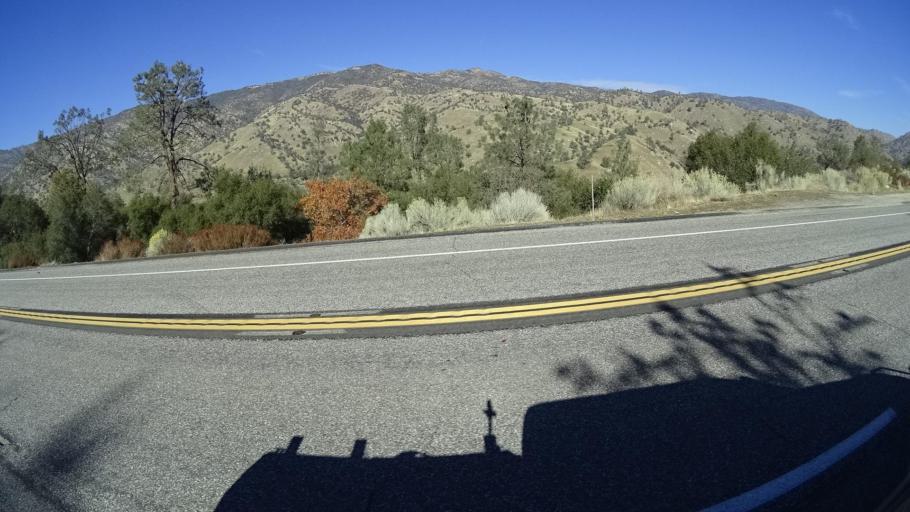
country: US
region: California
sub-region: Kern County
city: Bodfish
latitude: 35.5307
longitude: -118.6421
